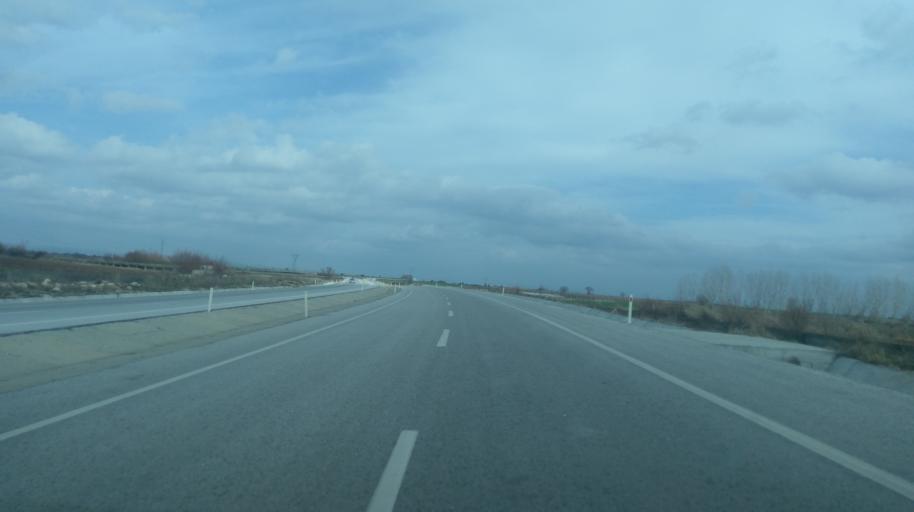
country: TR
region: Kirklareli
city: Inece
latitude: 41.6827
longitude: 27.1109
